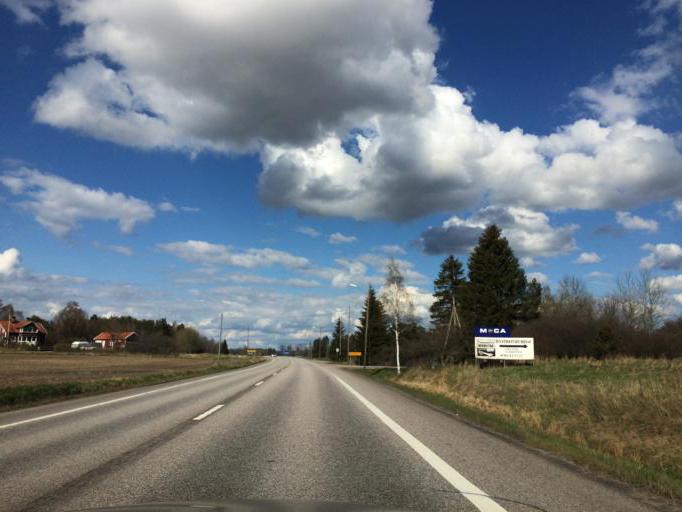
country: SE
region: Soedermanland
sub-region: Eskilstuna Kommun
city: Eskilstuna
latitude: 59.4068
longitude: 16.5767
